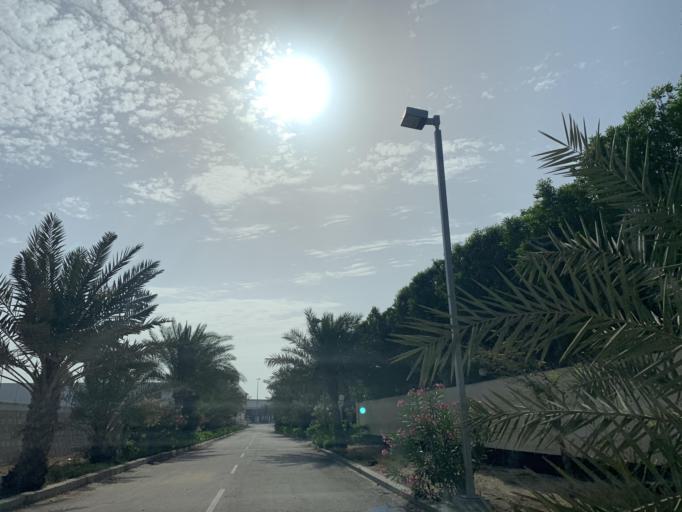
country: BH
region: Northern
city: Sitrah
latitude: 26.1584
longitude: 50.6038
